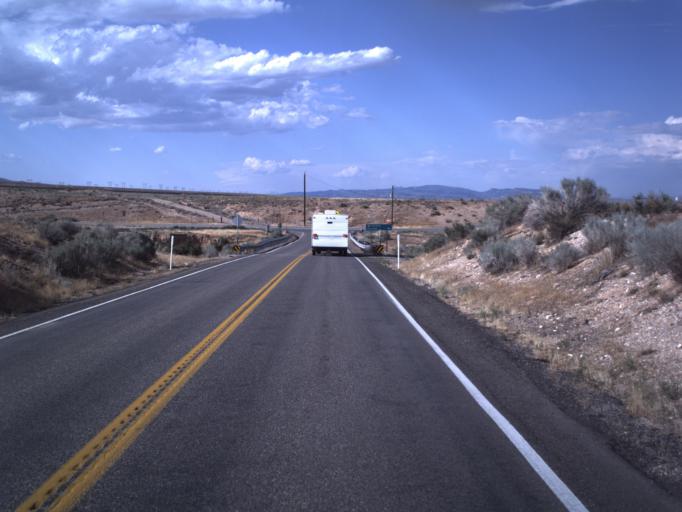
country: US
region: Utah
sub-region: Sevier County
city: Aurora
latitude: 38.9581
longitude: -111.9276
